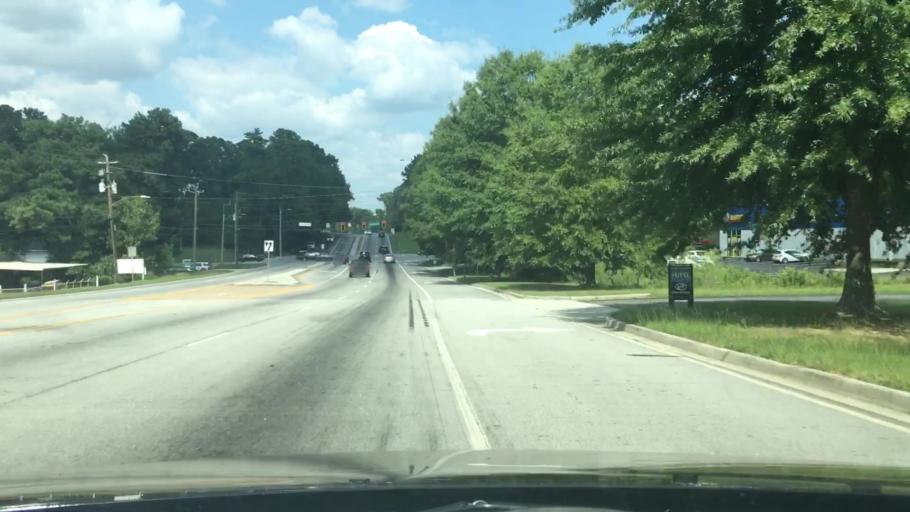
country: US
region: Georgia
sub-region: DeKalb County
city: Lithonia
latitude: 33.7132
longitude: -84.1257
